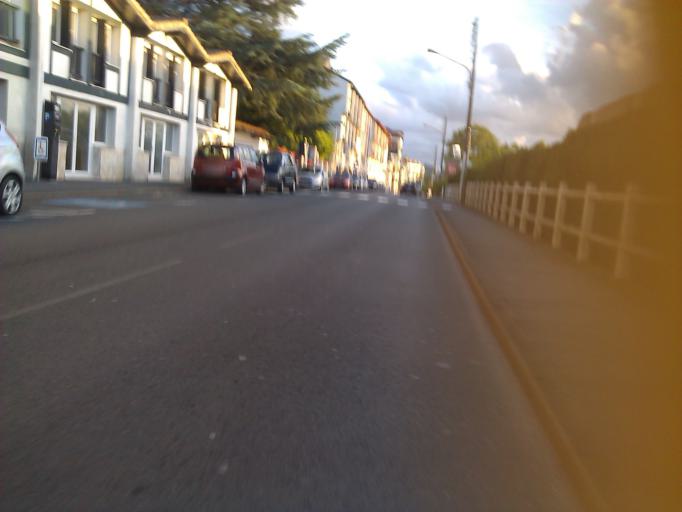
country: FR
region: Aquitaine
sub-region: Departement des Pyrenees-Atlantiques
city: Hendaye
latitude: 43.3549
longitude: -1.7788
